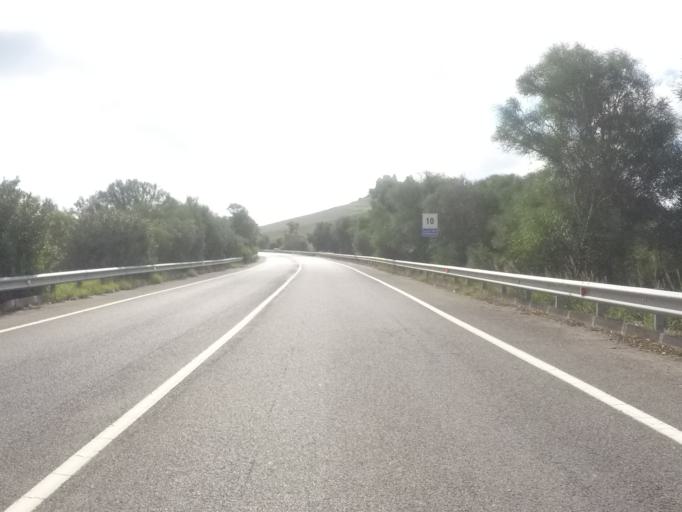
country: IT
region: Sicily
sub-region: Enna
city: Pietraperzia
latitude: 37.4479
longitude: 14.1166
